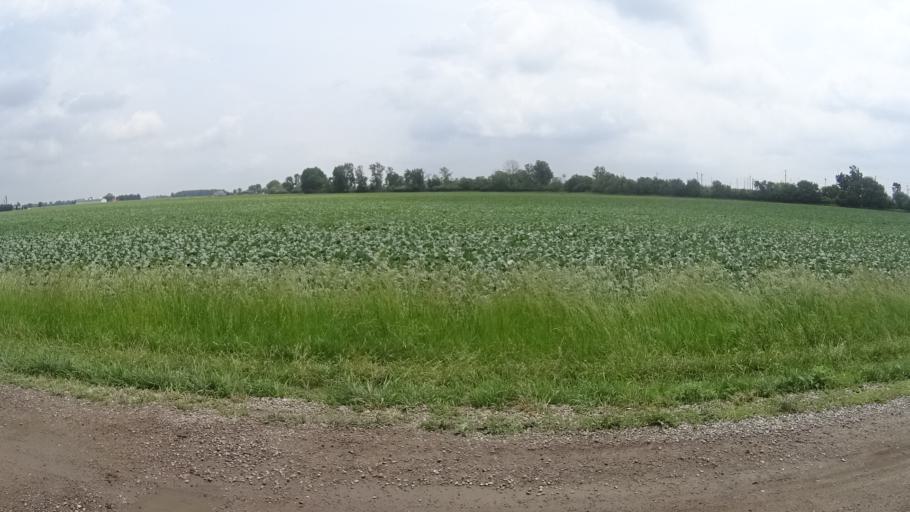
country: US
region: Ohio
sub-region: Huron County
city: Bellevue
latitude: 41.2937
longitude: -82.8043
